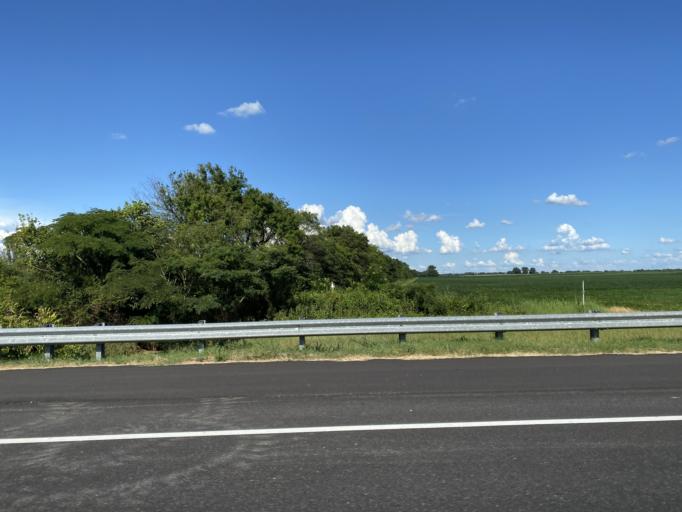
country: US
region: Alabama
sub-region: Limestone County
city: Athens
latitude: 34.7379
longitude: -86.9381
